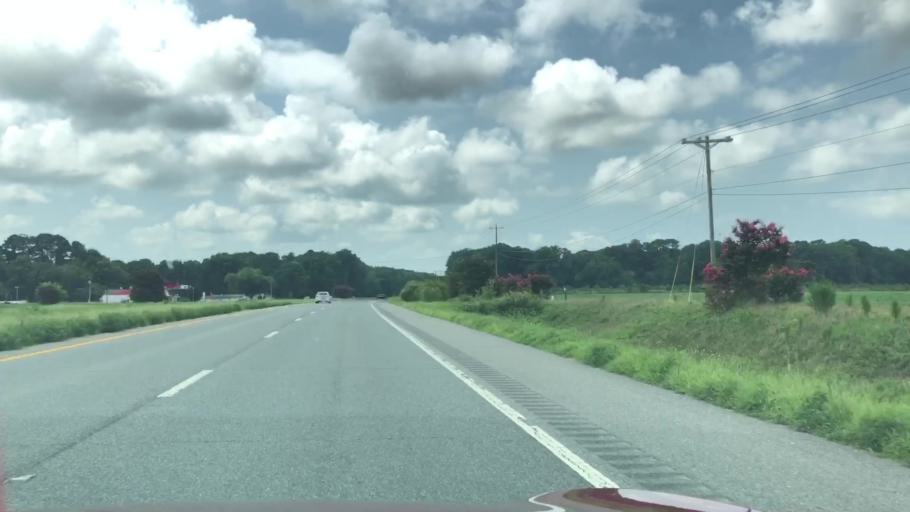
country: US
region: Virginia
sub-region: Northampton County
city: Eastville
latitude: 37.3239
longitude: -75.9505
